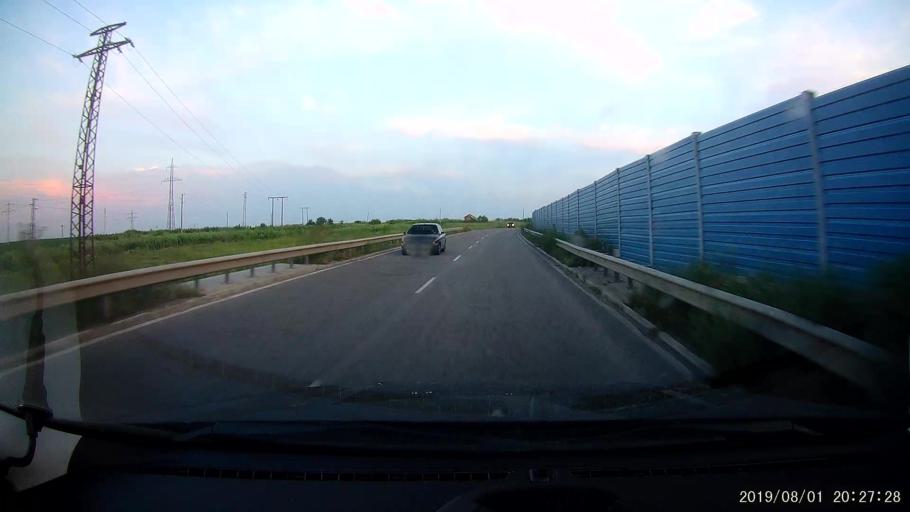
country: BG
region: Yambol
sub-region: Obshtina Elkhovo
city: Elkhovo
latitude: 42.1800
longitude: 26.5845
